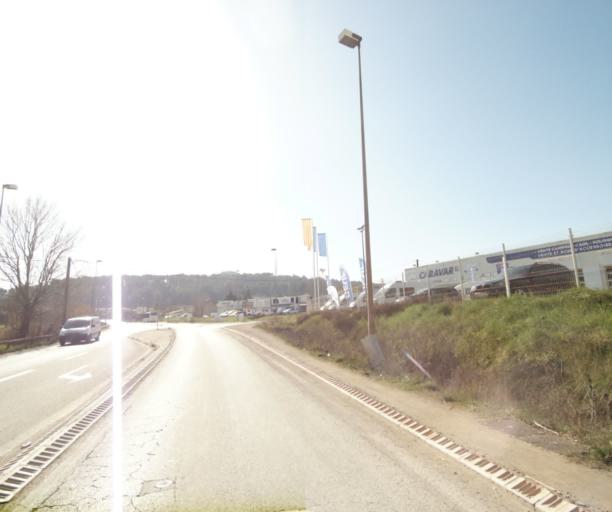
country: FR
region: Provence-Alpes-Cote d'Azur
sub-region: Departement des Bouches-du-Rhone
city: Gardanne
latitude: 43.4474
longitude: 5.4591
